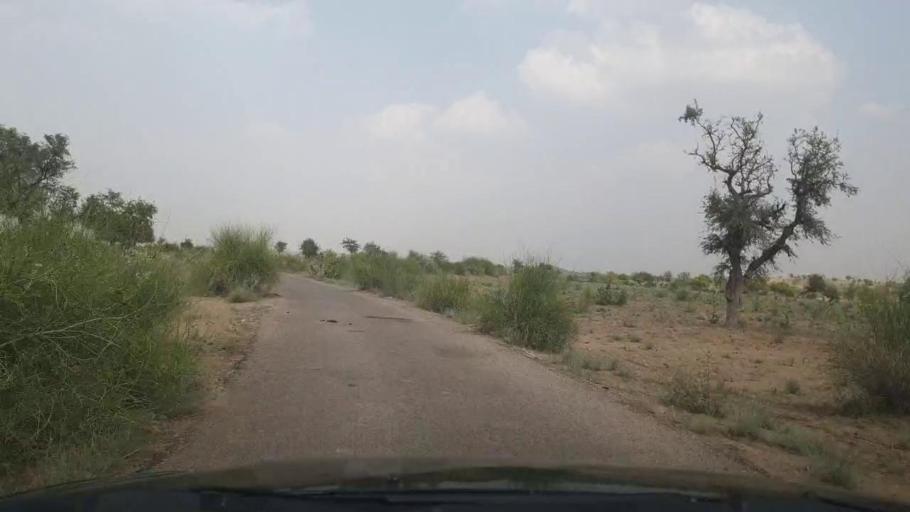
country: PK
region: Sindh
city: Islamkot
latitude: 24.9325
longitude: 70.5712
